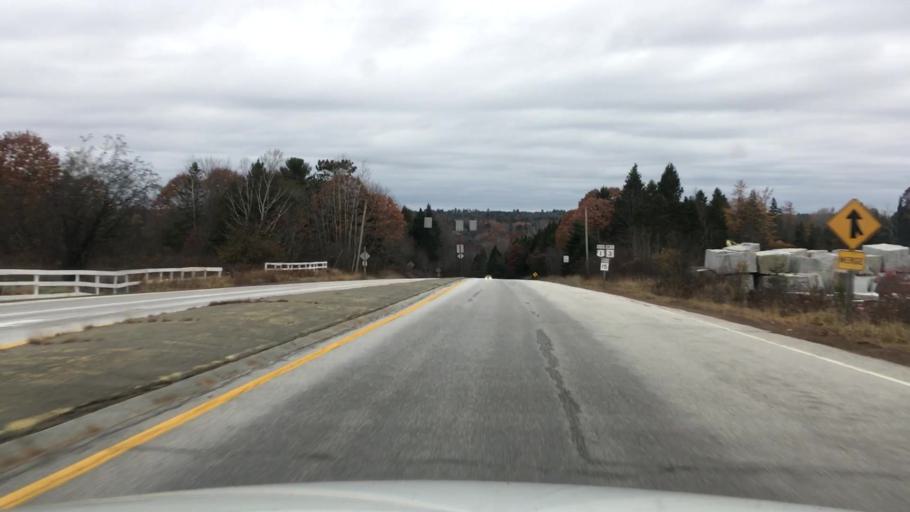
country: US
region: Maine
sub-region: Hancock County
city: Orland
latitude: 44.5743
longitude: -68.7319
